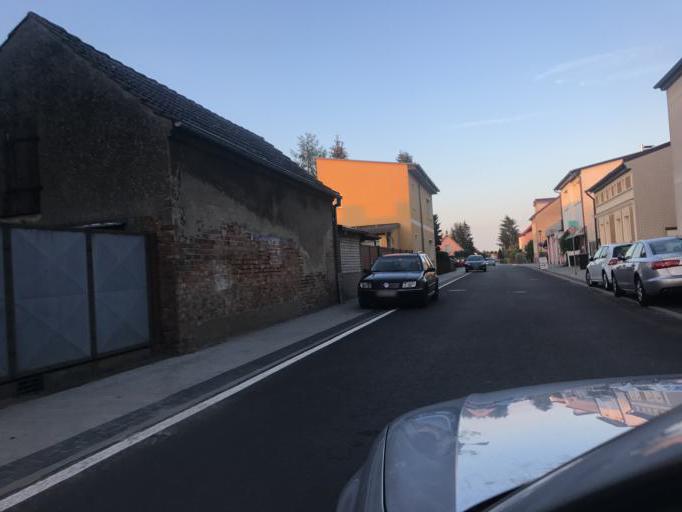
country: DE
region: Brandenburg
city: Melchow
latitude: 52.8518
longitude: 13.6824
